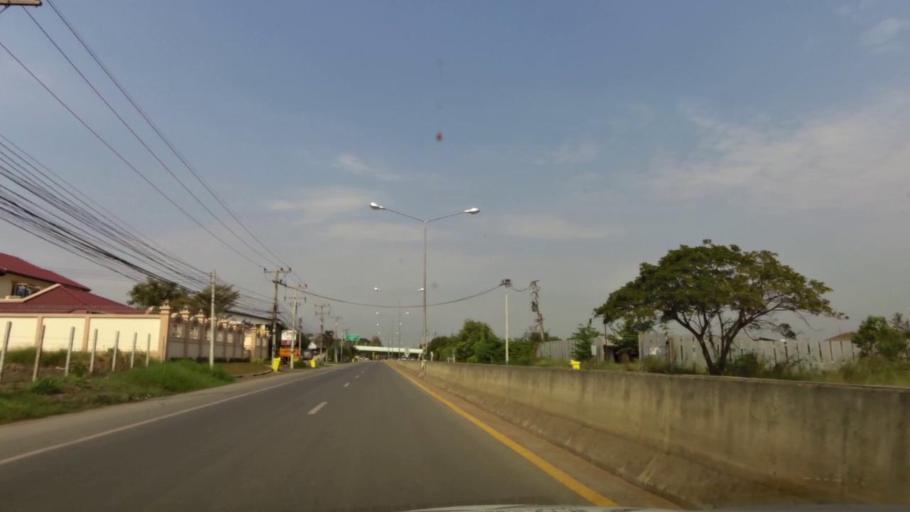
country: TH
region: Phra Nakhon Si Ayutthaya
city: Phra Nakhon Si Ayutthaya
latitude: 14.3288
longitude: 100.5768
